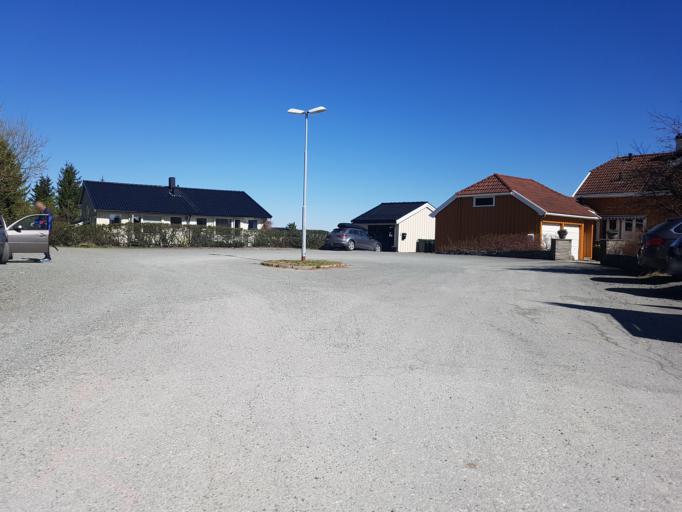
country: NO
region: Sor-Trondelag
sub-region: Trondheim
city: Trondheim
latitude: 63.4266
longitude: 10.3455
